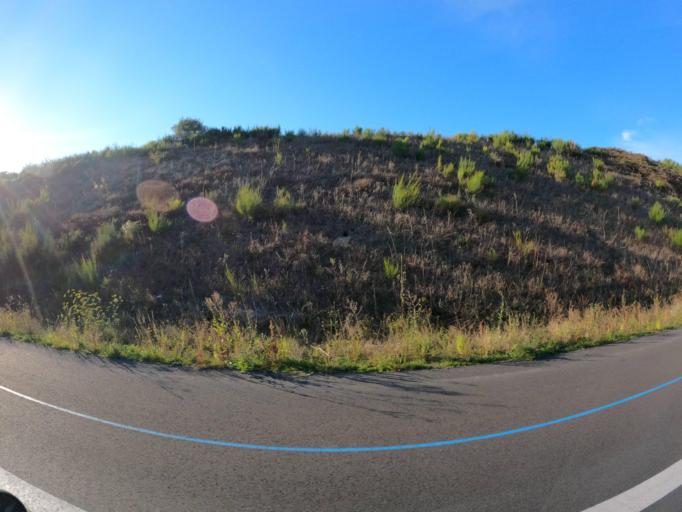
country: FR
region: Pays de la Loire
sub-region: Departement de la Vendee
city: Mortagne-sur-Sevre
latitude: 47.0042
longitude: -0.9044
